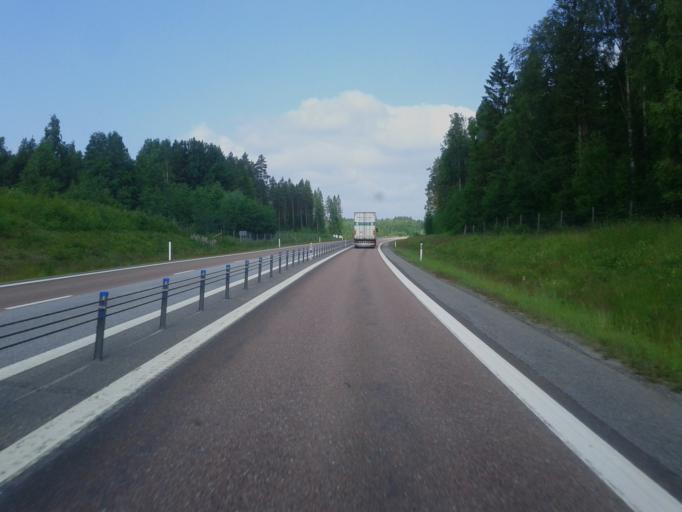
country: SE
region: Vaesterbotten
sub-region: Skelleftea Kommun
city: Skelleftea
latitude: 64.7186
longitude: 20.9877
